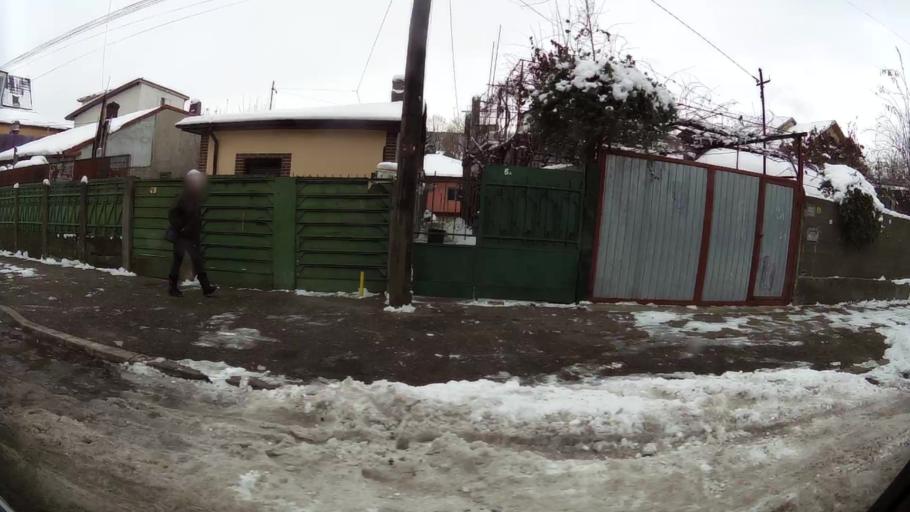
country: RO
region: Bucuresti
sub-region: Municipiul Bucuresti
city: Bucuresti
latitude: 44.3956
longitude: 26.1010
